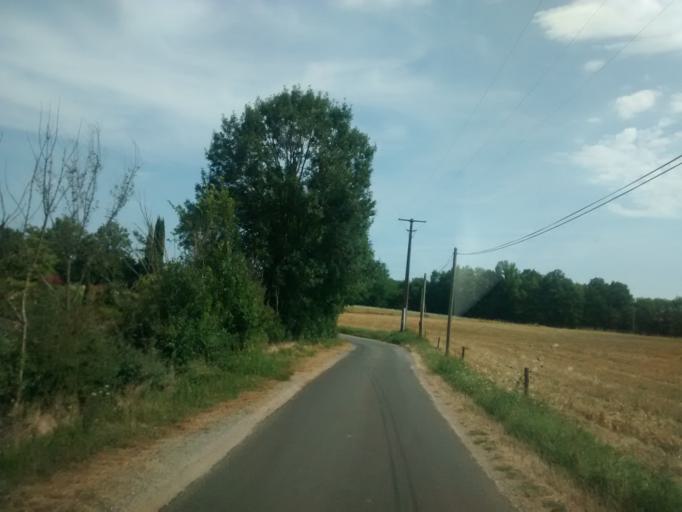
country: FR
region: Aquitaine
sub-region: Departement de la Dordogne
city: Cenac-et-Saint-Julien
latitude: 44.8013
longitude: 1.1399
